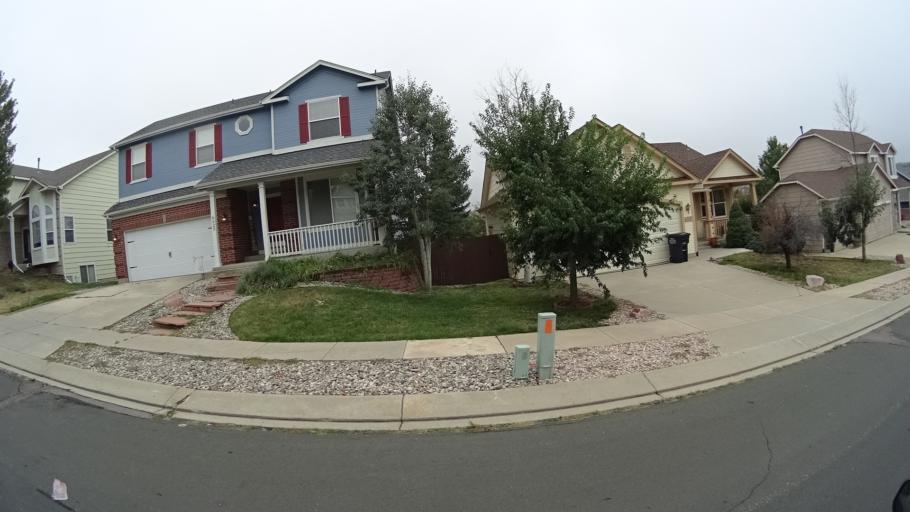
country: US
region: Colorado
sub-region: El Paso County
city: Cimarron Hills
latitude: 38.9306
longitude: -104.7486
